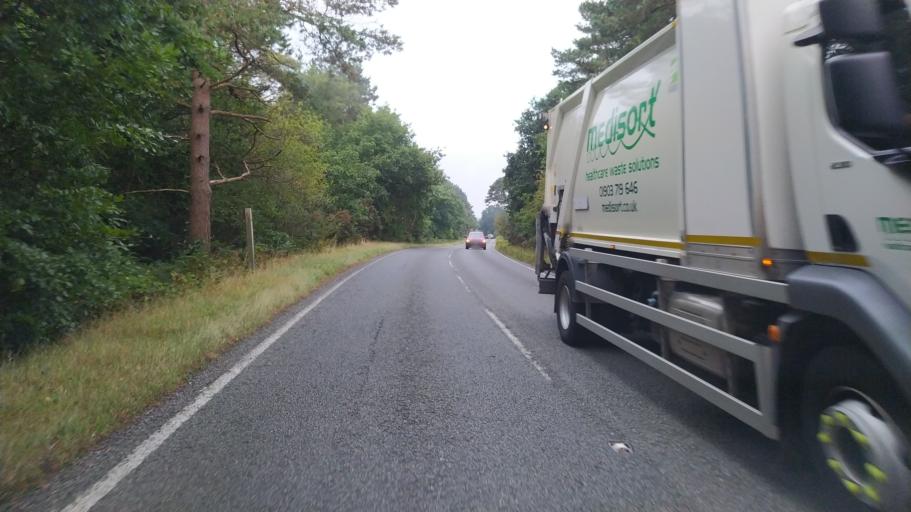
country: GB
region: England
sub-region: Hampshire
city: New Milton
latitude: 50.8097
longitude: -1.6654
